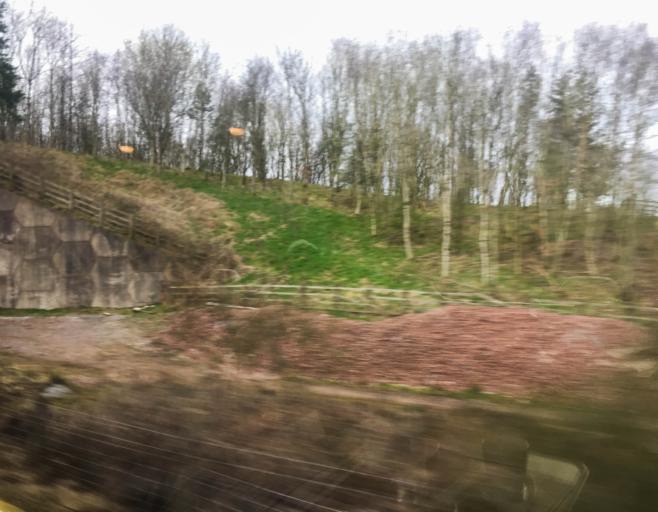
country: GB
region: Scotland
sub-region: Dumfries and Galloway
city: Moffat
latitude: 55.2915
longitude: -3.4387
